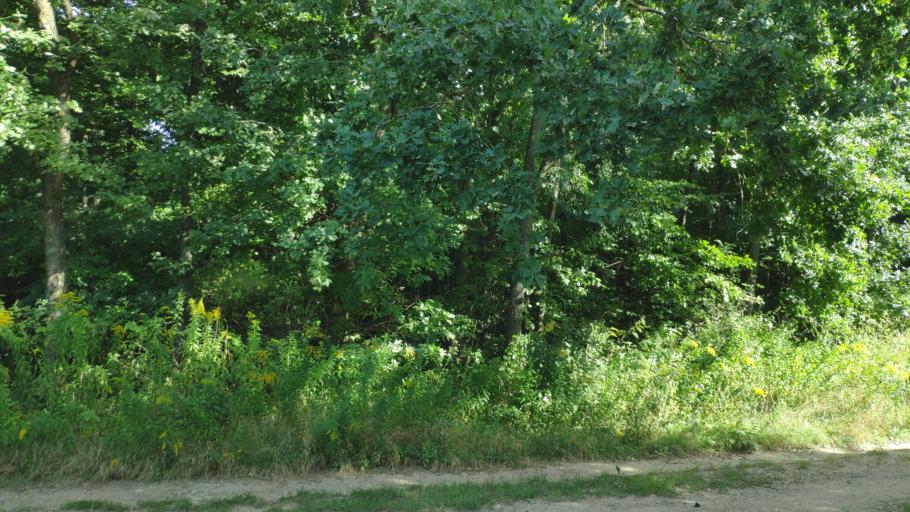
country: SK
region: Kosicky
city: Kosice
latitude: 48.7685
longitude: 21.2489
